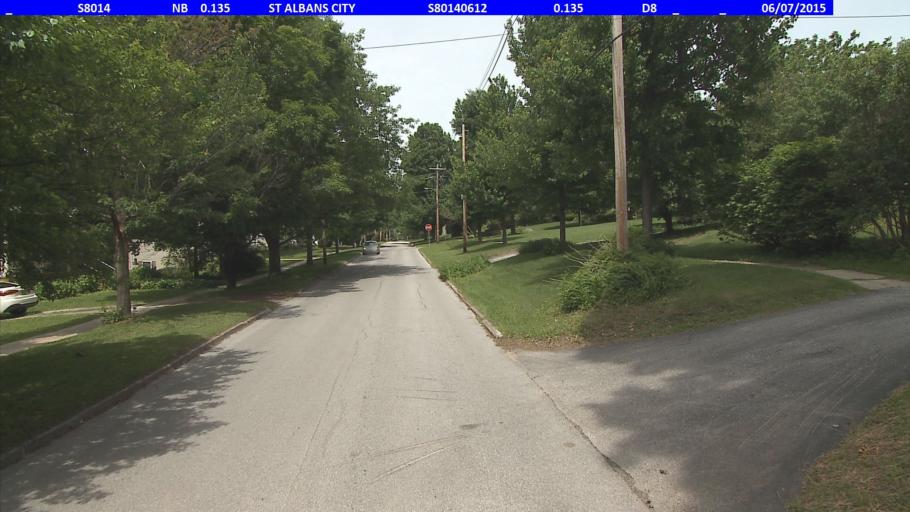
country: US
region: Vermont
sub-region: Franklin County
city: Saint Albans
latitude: 44.8153
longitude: -73.0776
